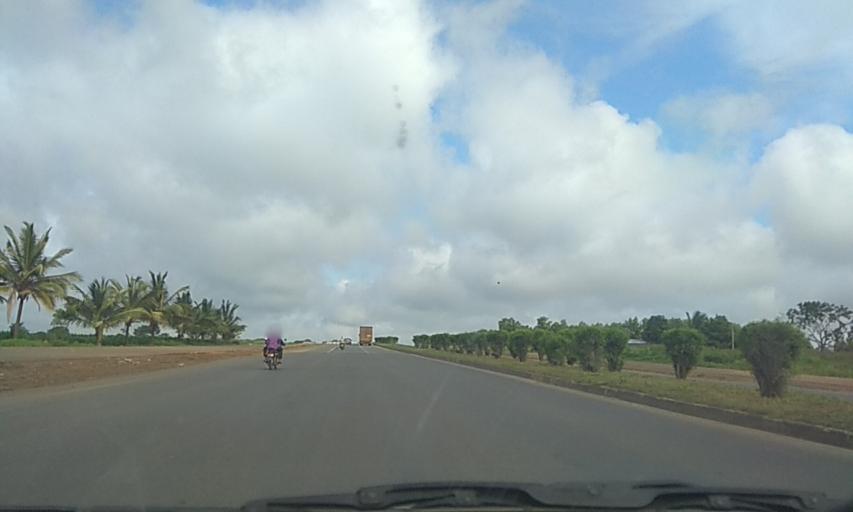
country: IN
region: Karnataka
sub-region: Haveri
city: Shiggaon
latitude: 15.0056
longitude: 75.2023
